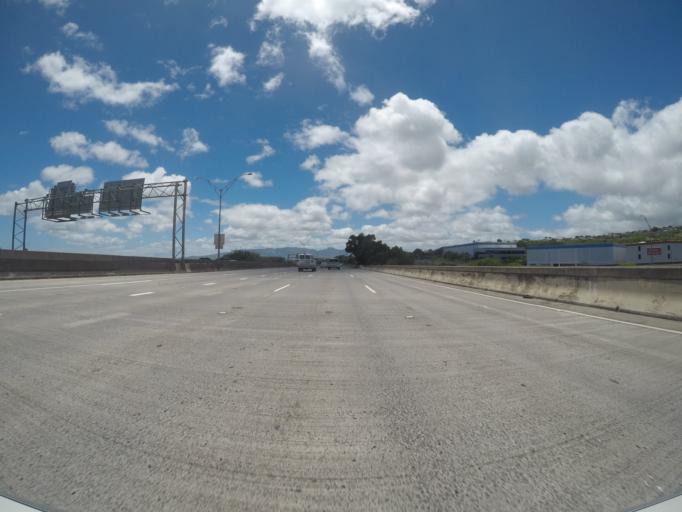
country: US
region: Hawaii
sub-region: Honolulu County
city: Halawa Heights
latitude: 21.3703
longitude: -157.9141
